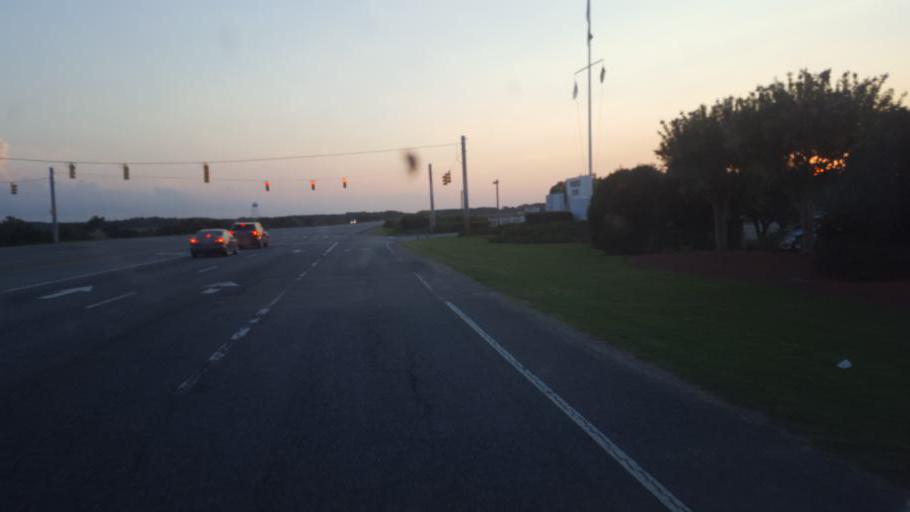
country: US
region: North Carolina
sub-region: Dare County
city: Manteo
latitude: 35.8930
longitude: -75.6437
